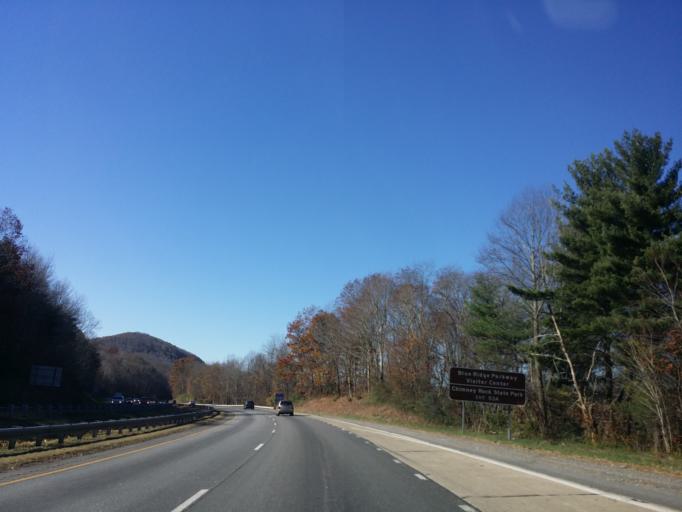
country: US
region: North Carolina
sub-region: Buncombe County
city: Swannanoa
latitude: 35.5789
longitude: -82.4706
